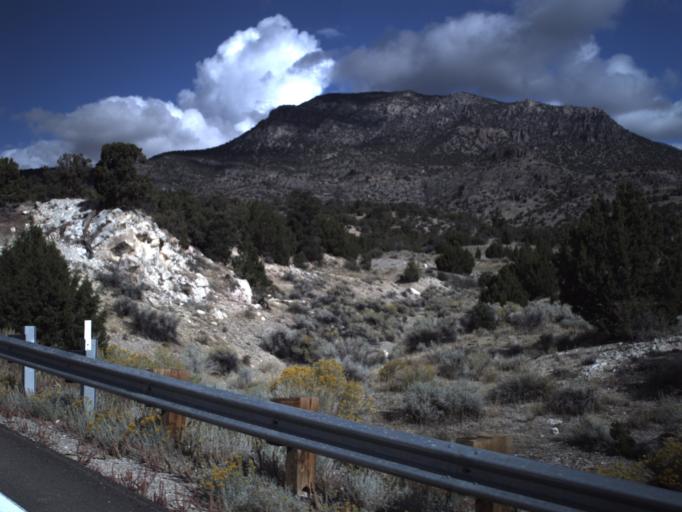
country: US
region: Utah
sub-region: Beaver County
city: Milford
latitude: 38.5164
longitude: -113.5363
